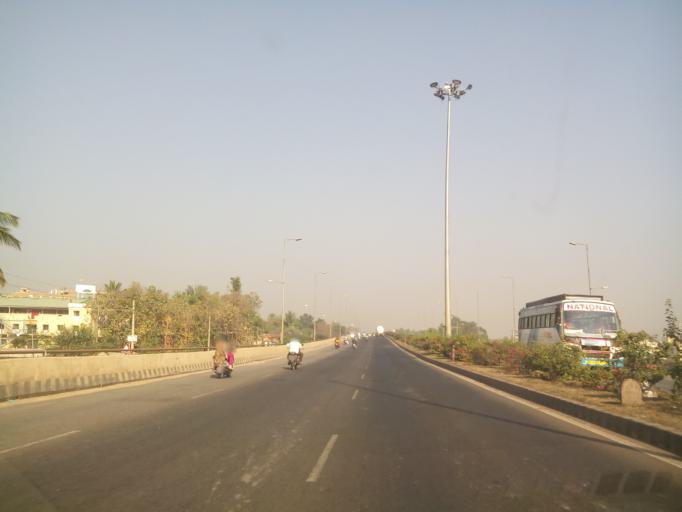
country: IN
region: Karnataka
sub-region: Bangalore Rural
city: Nelamangala
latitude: 13.0810
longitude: 77.4216
